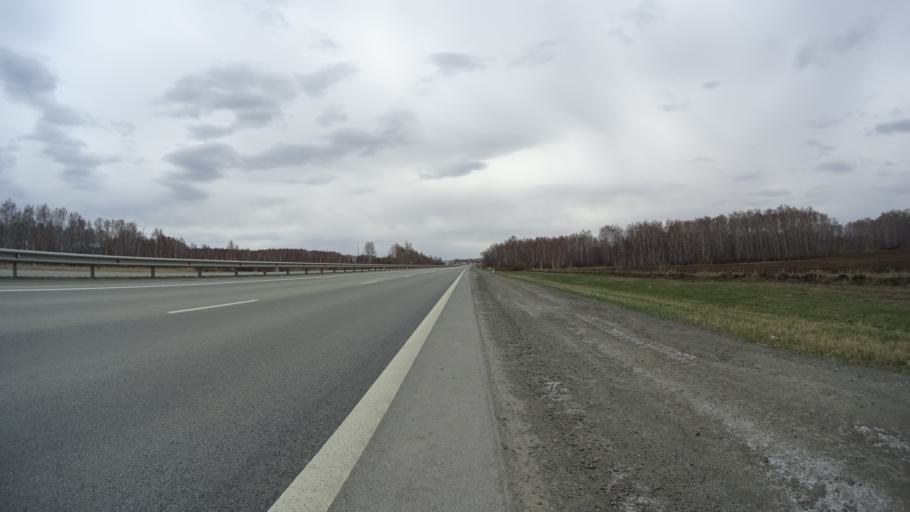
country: RU
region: Chelyabinsk
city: Yemanzhelinka
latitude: 54.8299
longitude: 61.3113
